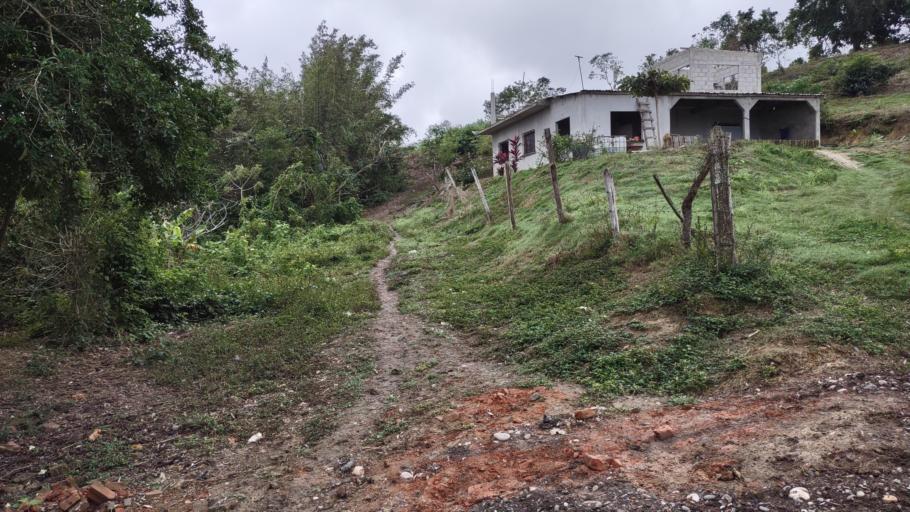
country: MX
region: Veracruz
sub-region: Papantla
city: El Chote
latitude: 20.3935
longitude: -97.3933
